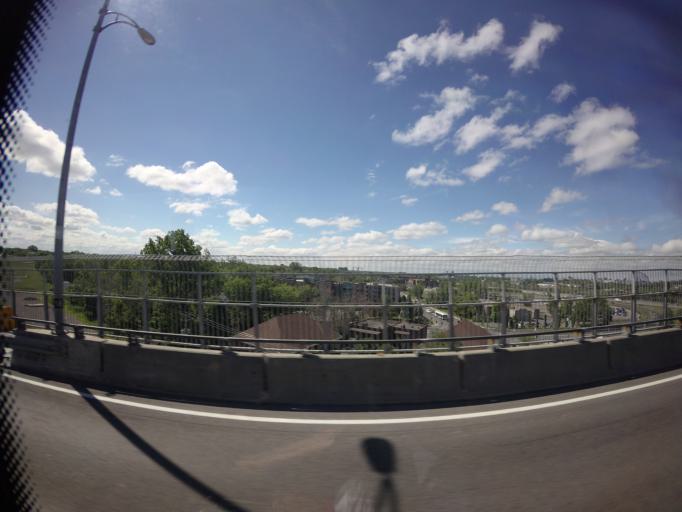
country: CA
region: Quebec
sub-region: Monteregie
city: Longueuil
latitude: 45.5221
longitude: -73.5197
